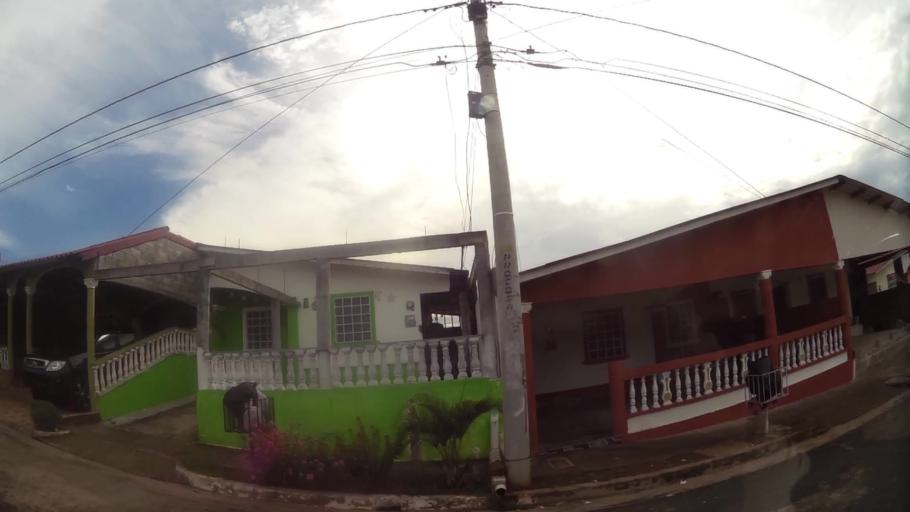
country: PA
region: Panama
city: La Chorrera
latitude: 8.8867
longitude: -79.7561
